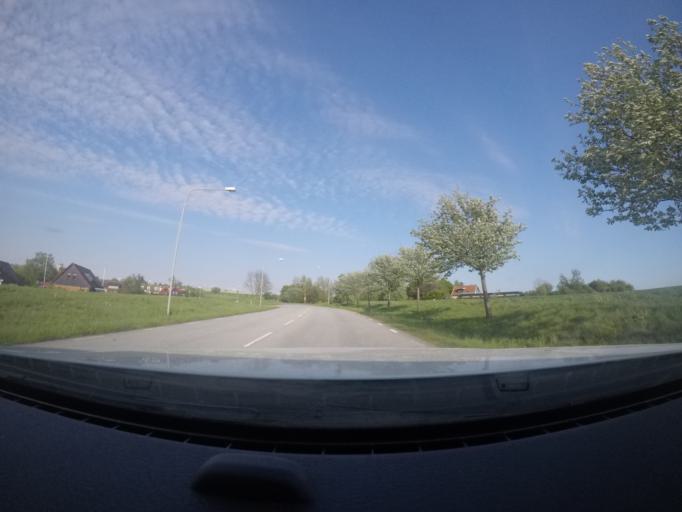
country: SE
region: Skane
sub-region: Helsingborg
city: Glumslov
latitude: 55.9361
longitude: 12.8095
